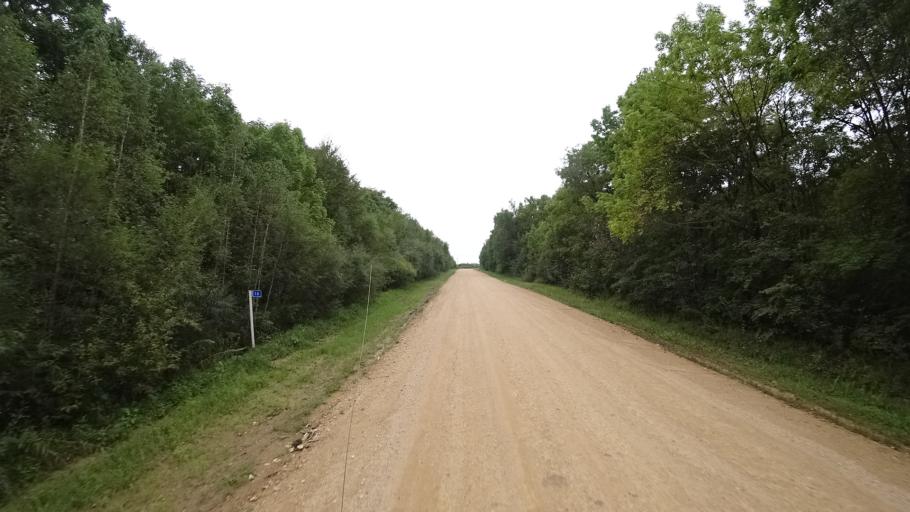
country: RU
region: Primorskiy
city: Monastyrishche
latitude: 44.0833
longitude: 132.5952
